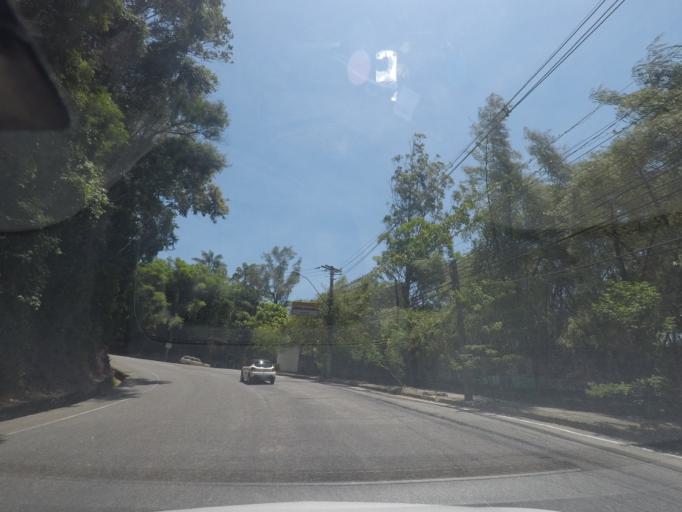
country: BR
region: Rio de Janeiro
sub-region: Niteroi
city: Niteroi
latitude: -22.9166
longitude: -43.0652
